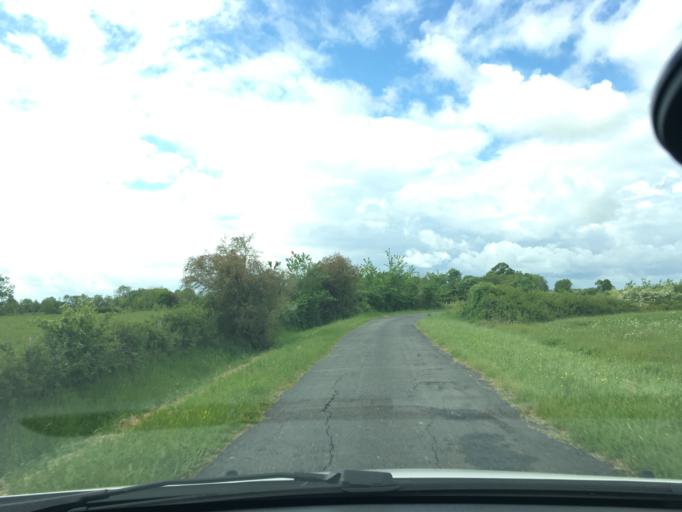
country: FR
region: Aquitaine
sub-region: Departement de la Gironde
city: Saint-Estephe
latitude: 45.3302
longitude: -0.8035
